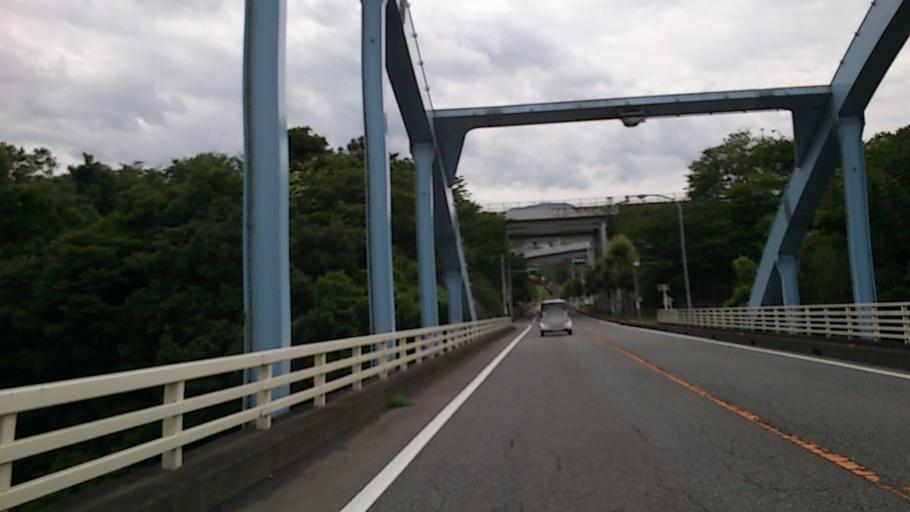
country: JP
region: Gunma
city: Tomioka
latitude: 36.2375
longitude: 138.8231
